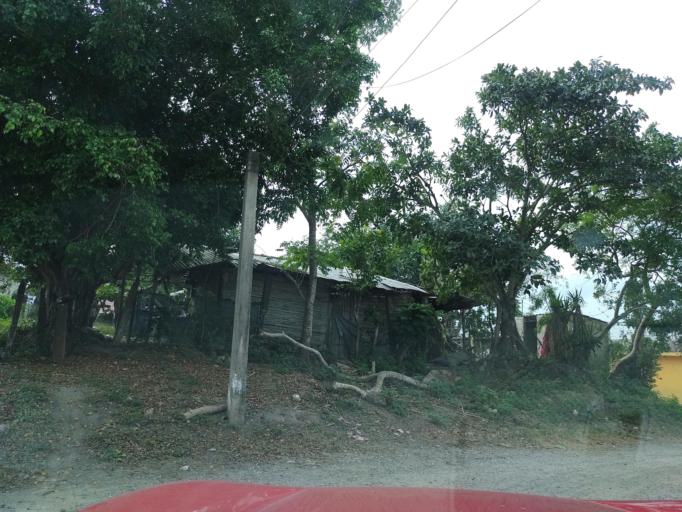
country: MX
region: Veracruz
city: Agua Dulce
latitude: 20.3636
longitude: -97.2972
